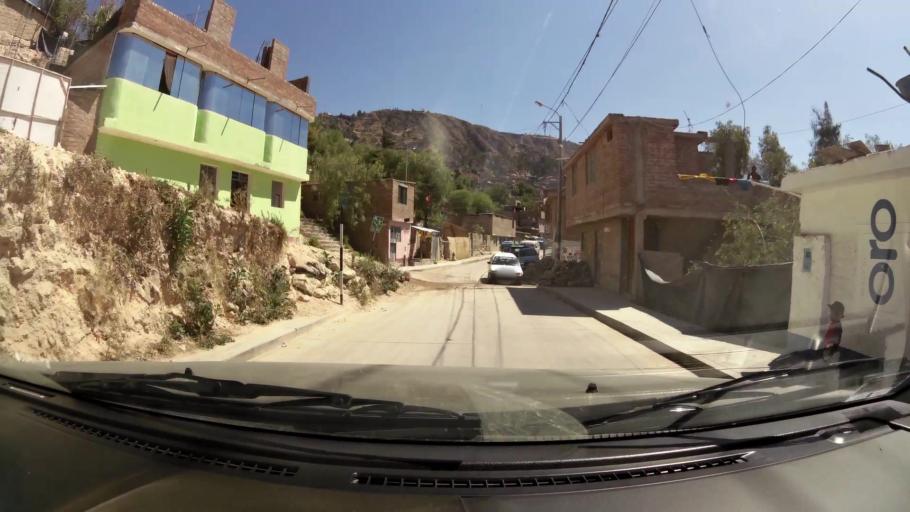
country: PE
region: Ayacucho
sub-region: Provincia de Huamanga
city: Ayacucho
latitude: -13.1657
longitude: -74.2357
